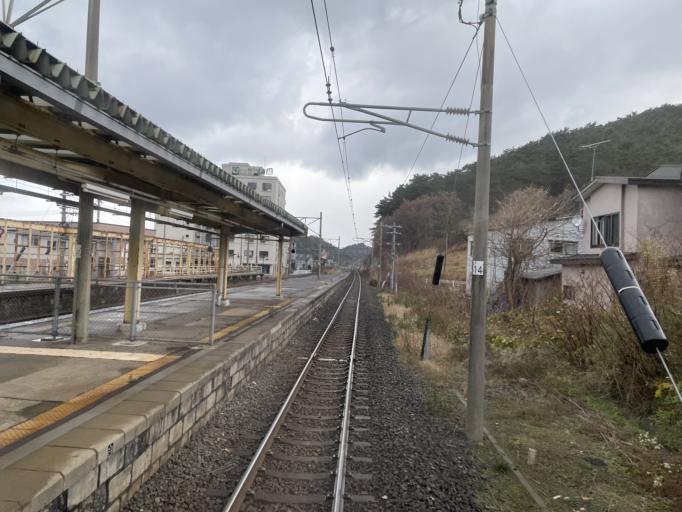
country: JP
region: Aomori
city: Aomori Shi
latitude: 40.8919
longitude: 140.8624
